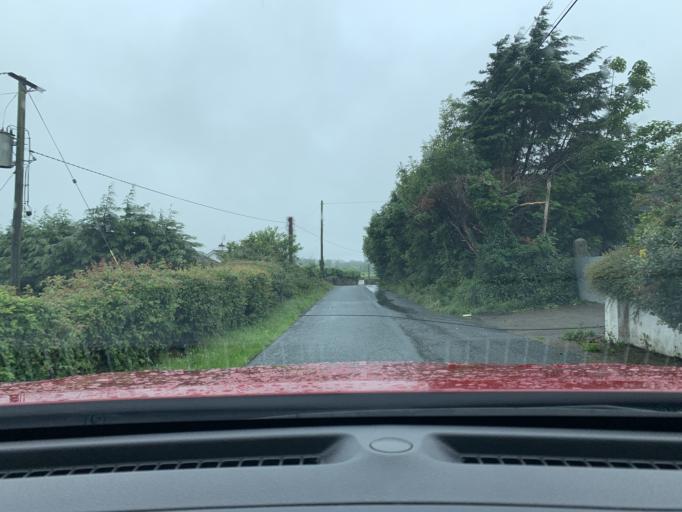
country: IE
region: Connaught
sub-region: Sligo
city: Sligo
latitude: 54.3081
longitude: -8.4722
